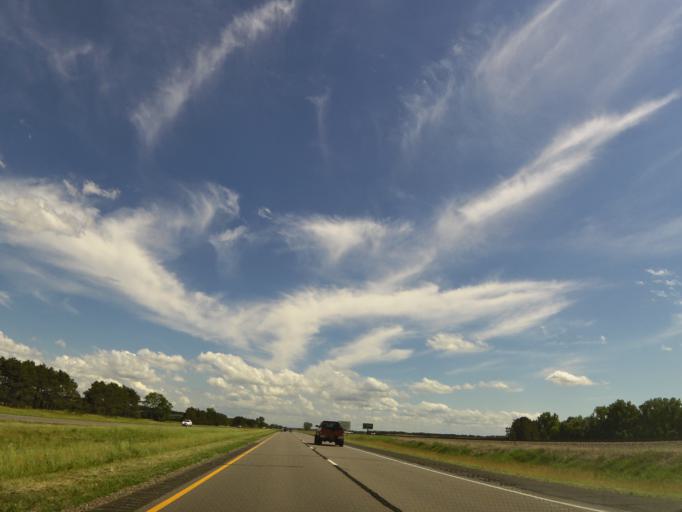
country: US
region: Minnesota
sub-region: Benton County
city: Rice
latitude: 45.7386
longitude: -94.2068
